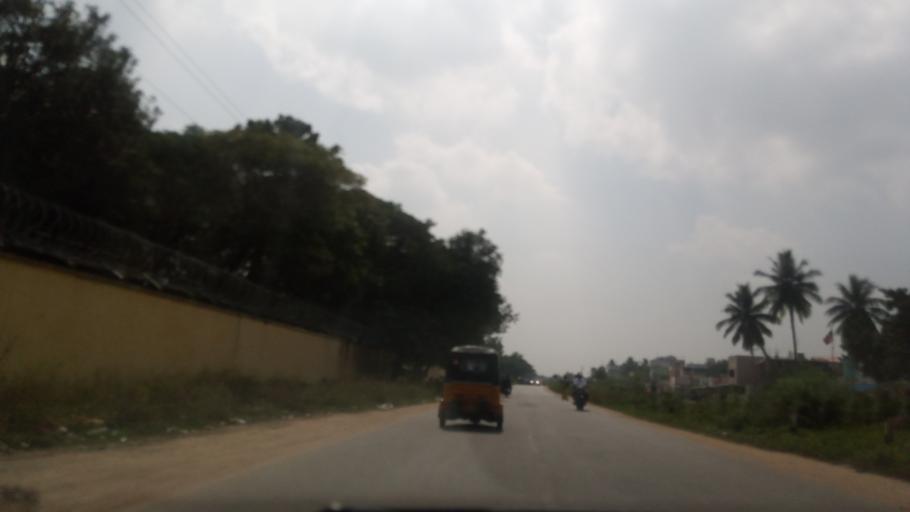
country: IN
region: Tamil Nadu
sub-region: Vellore
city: Arakkonam
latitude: 13.0670
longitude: 79.6731
